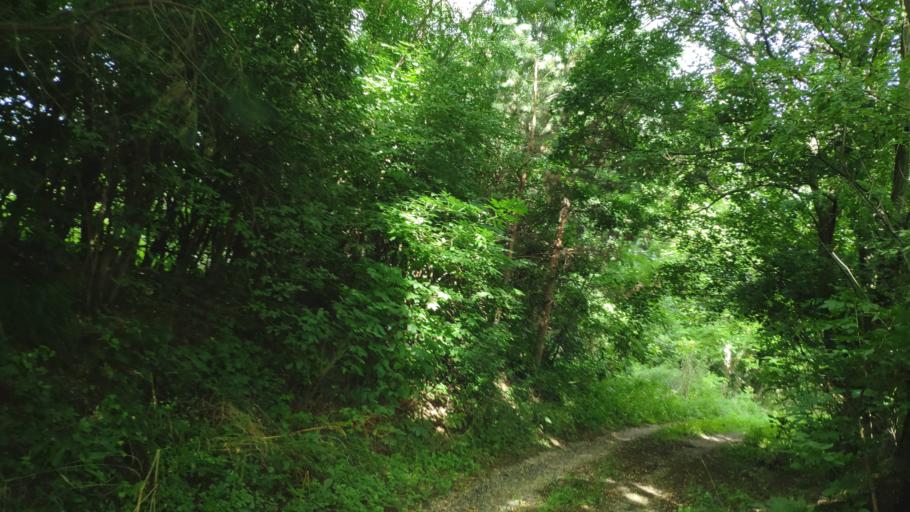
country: SK
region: Kosicky
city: Secovce
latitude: 48.6064
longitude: 21.5473
